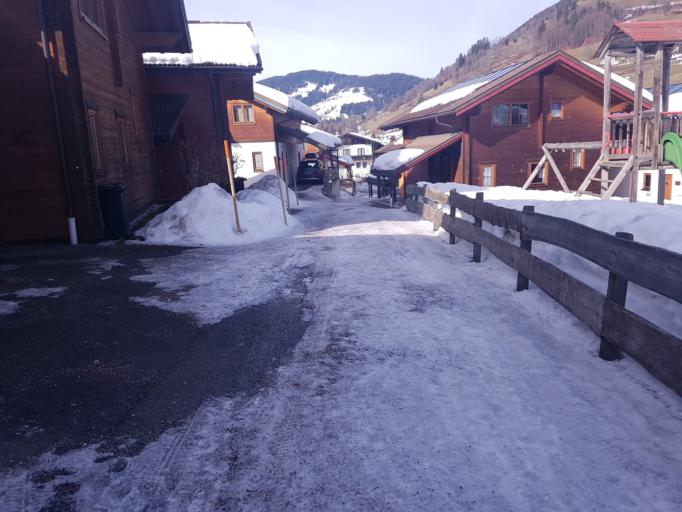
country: AT
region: Tyrol
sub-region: Politischer Bezirk Kufstein
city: Worgl
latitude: 47.4504
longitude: 12.0898
